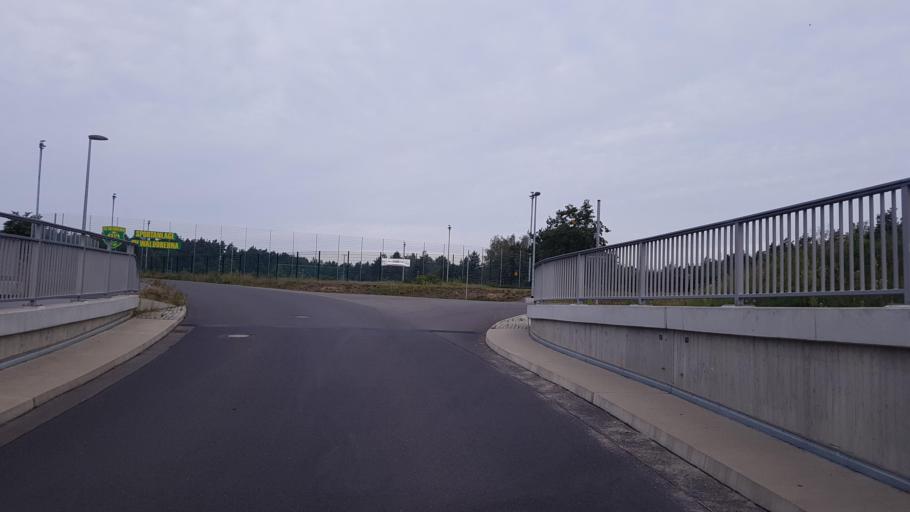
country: DE
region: Brandenburg
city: Sonnewalde
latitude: 51.7791
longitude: 13.6189
